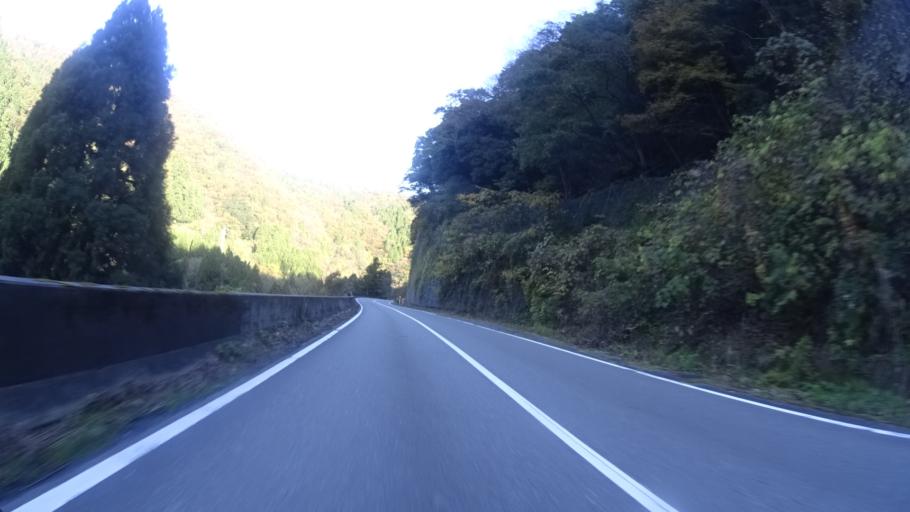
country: JP
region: Fukui
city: Maruoka
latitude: 36.2162
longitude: 136.3527
